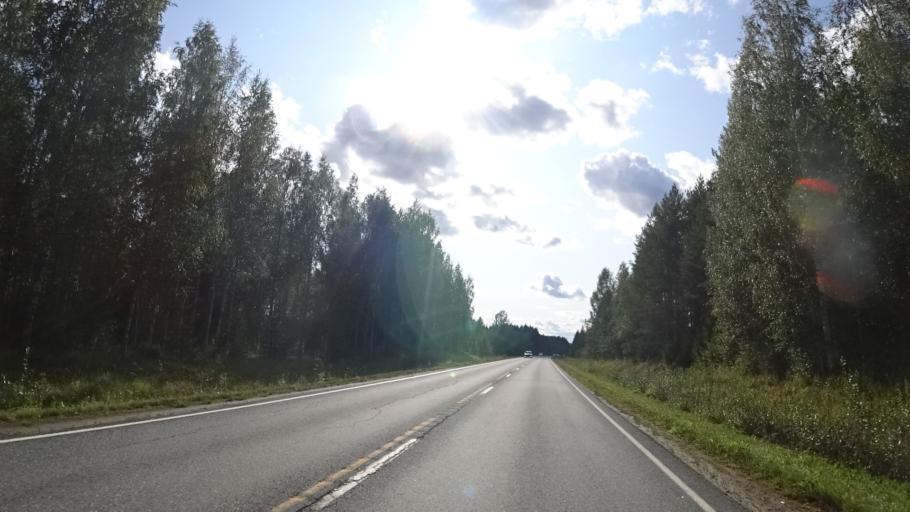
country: FI
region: North Karelia
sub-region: Keski-Karjala
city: Kitee
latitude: 62.0928
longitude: 30.0504
